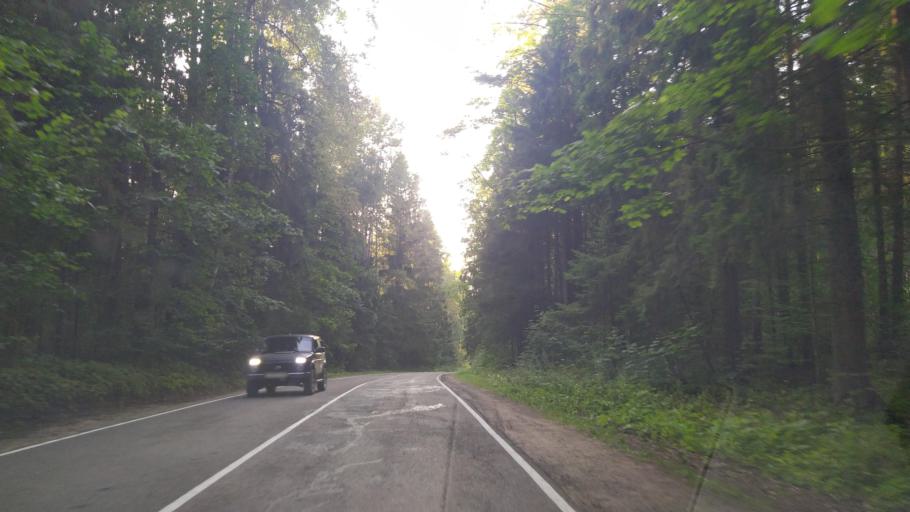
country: RU
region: Pskov
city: Pushkinskiye Gory
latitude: 57.0357
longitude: 28.9144
